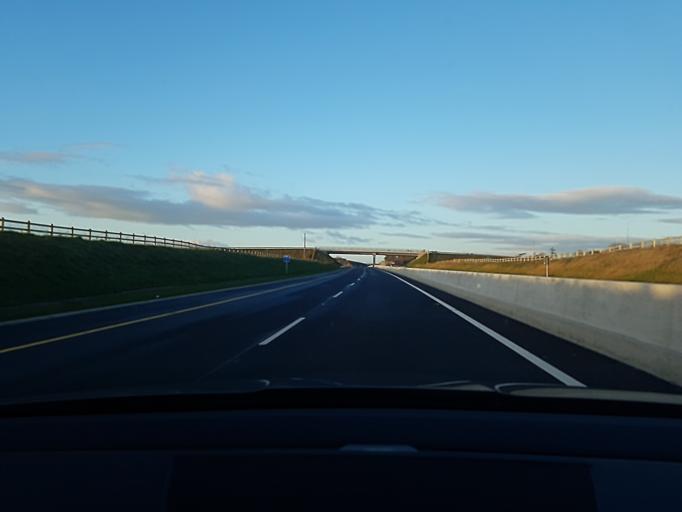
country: IE
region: Connaught
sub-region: County Galway
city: Athenry
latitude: 53.3363
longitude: -8.8023
